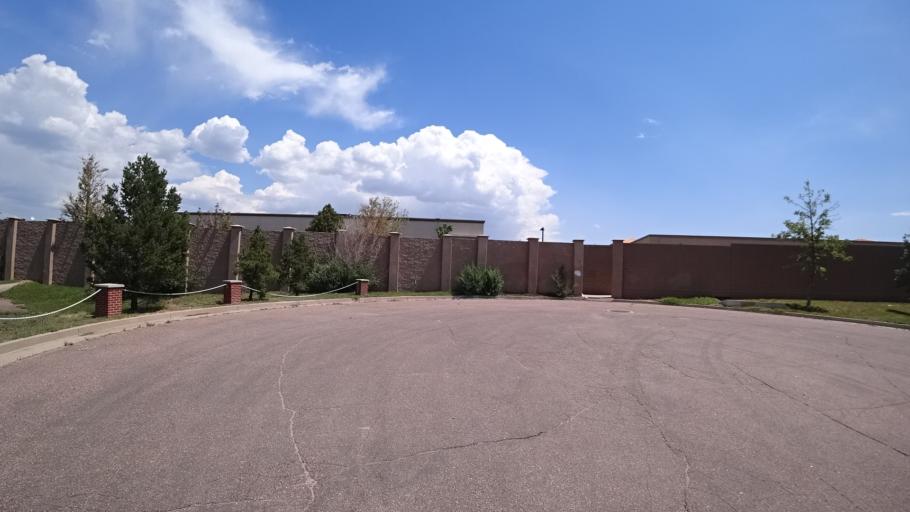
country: US
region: Colorado
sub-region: El Paso County
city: Air Force Academy
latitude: 38.9371
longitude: -104.7997
